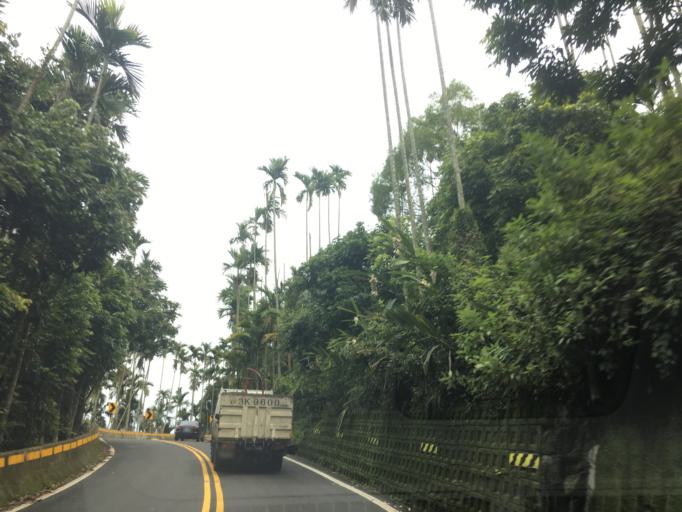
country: TW
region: Taiwan
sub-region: Yunlin
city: Douliu
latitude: 23.5575
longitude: 120.5859
